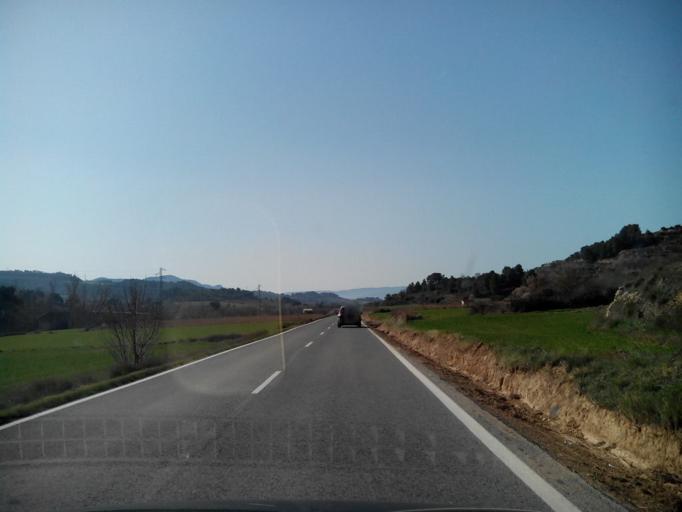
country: ES
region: Catalonia
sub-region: Provincia de Tarragona
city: Fores
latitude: 41.4633
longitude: 1.2686
